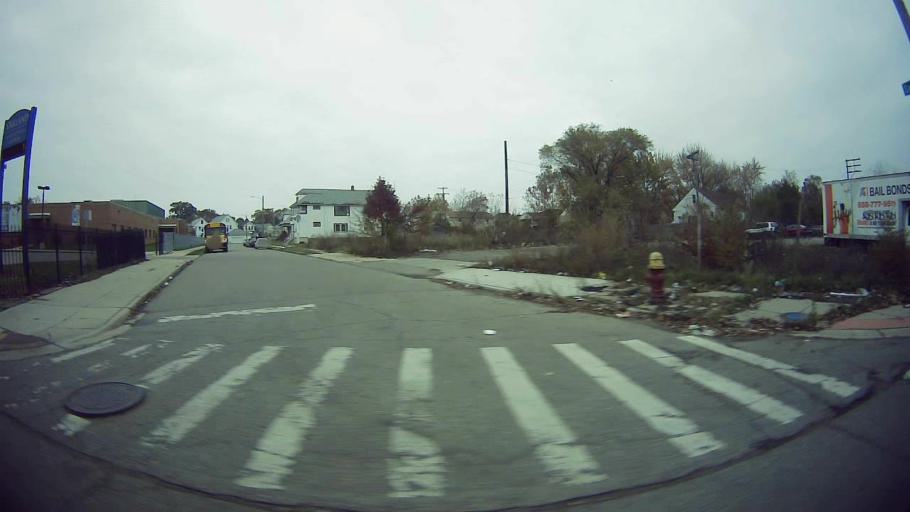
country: US
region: Michigan
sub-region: Wayne County
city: Hamtramck
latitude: 42.3890
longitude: -83.0427
